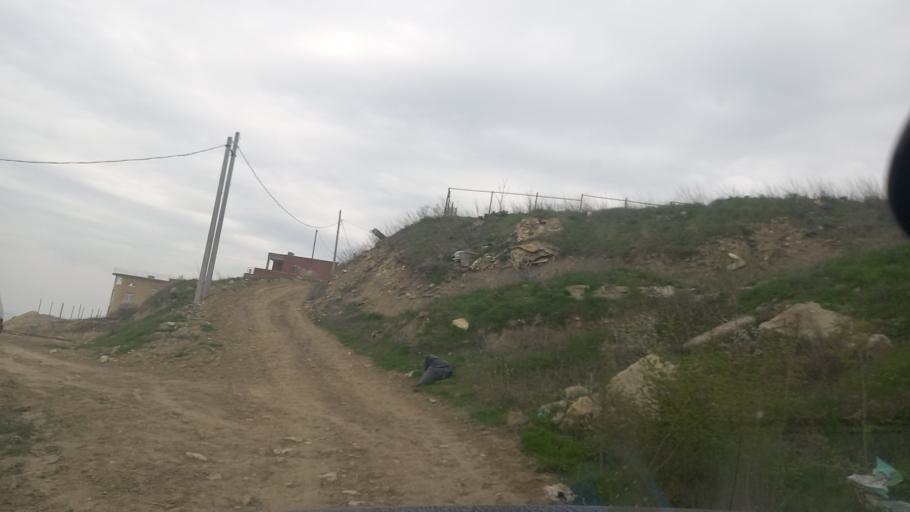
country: RU
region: Krasnodarskiy
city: Anapa
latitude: 44.8544
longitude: 37.3408
